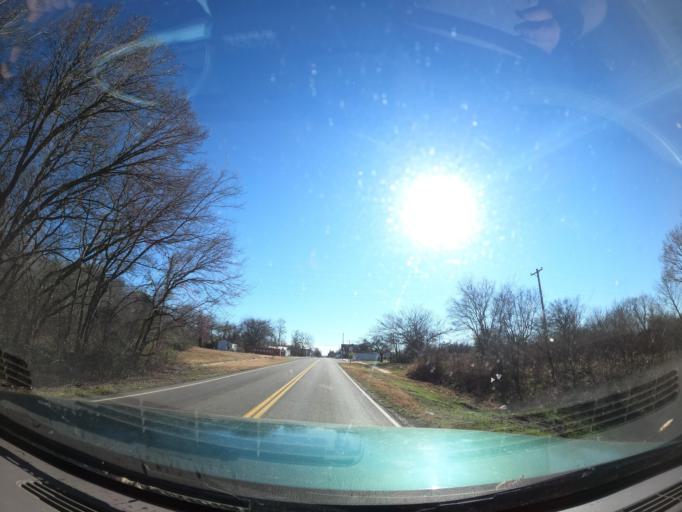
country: US
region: Oklahoma
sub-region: Muskogee County
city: Haskell
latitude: 35.6506
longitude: -95.6561
